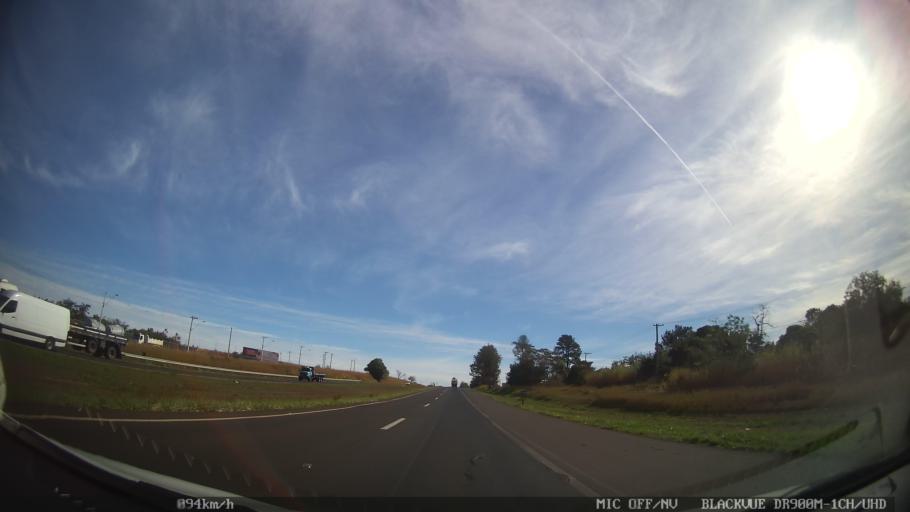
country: BR
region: Sao Paulo
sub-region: Sao Jose Do Rio Preto
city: Sao Jose do Rio Preto
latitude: -20.7970
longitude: -49.3232
